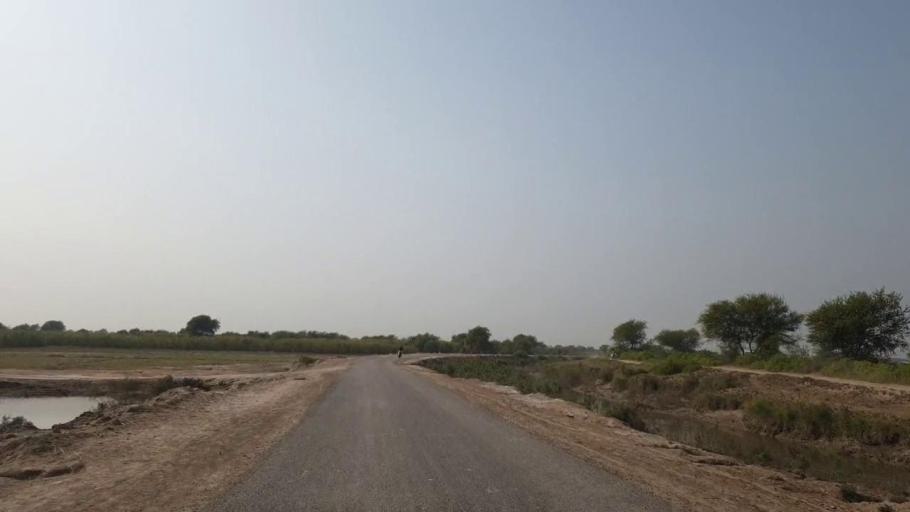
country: PK
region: Sindh
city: Matli
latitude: 24.9614
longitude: 68.5192
